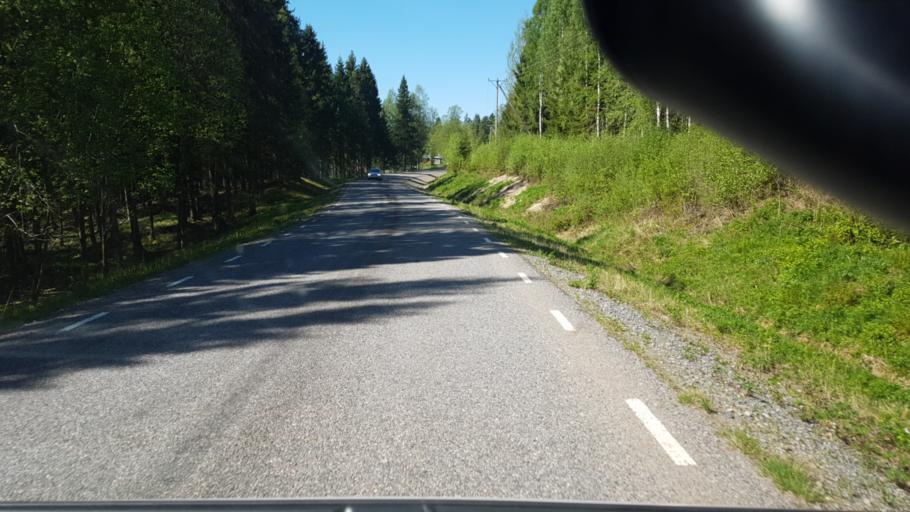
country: SE
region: Vaermland
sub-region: Eda Kommun
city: Charlottenberg
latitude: 59.9787
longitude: 12.4000
